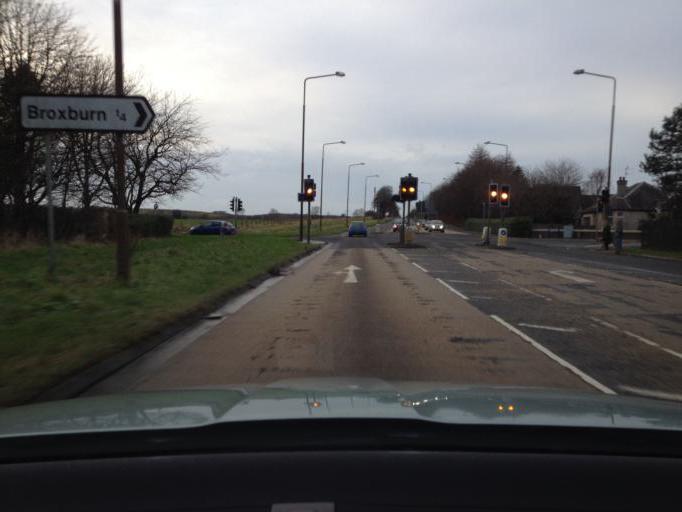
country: GB
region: Scotland
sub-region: West Lothian
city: Broxburn
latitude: 55.9307
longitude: -3.4688
